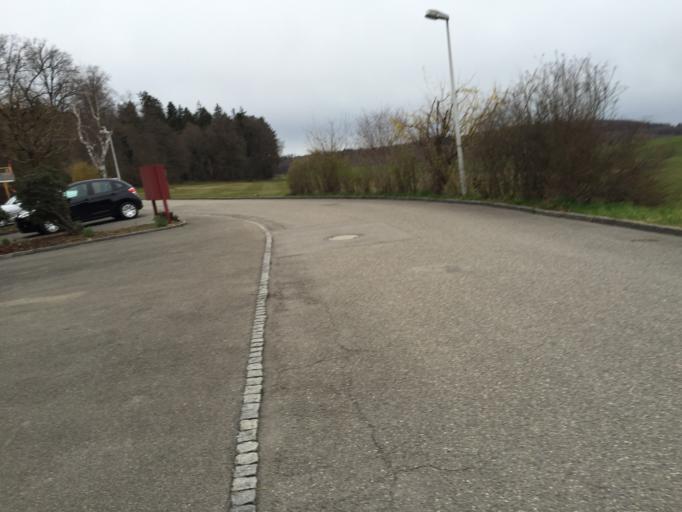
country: CH
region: Bern
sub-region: Bern-Mittelland District
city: Koniz
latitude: 46.9141
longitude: 7.4155
